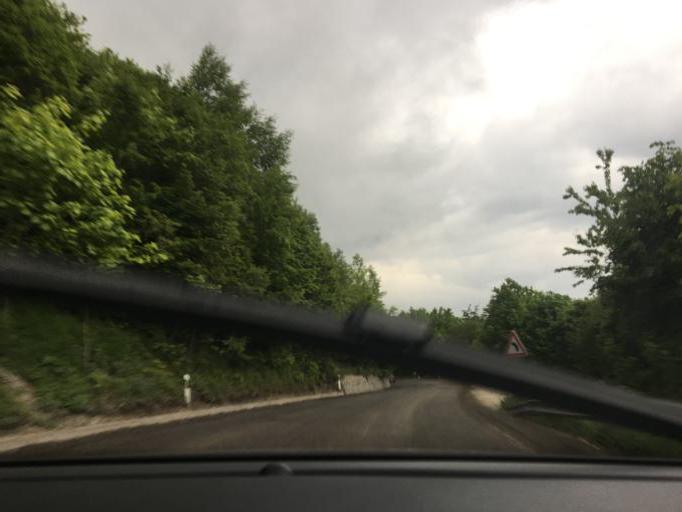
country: MK
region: Gostivar
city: Vrutok
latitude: 41.6726
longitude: 20.8530
